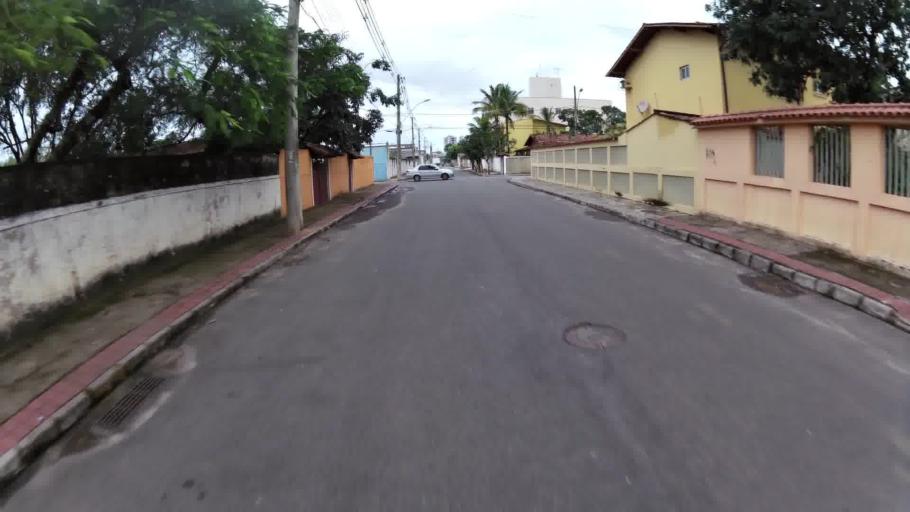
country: BR
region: Espirito Santo
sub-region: Guarapari
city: Guarapari
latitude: -20.6514
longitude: -40.4917
